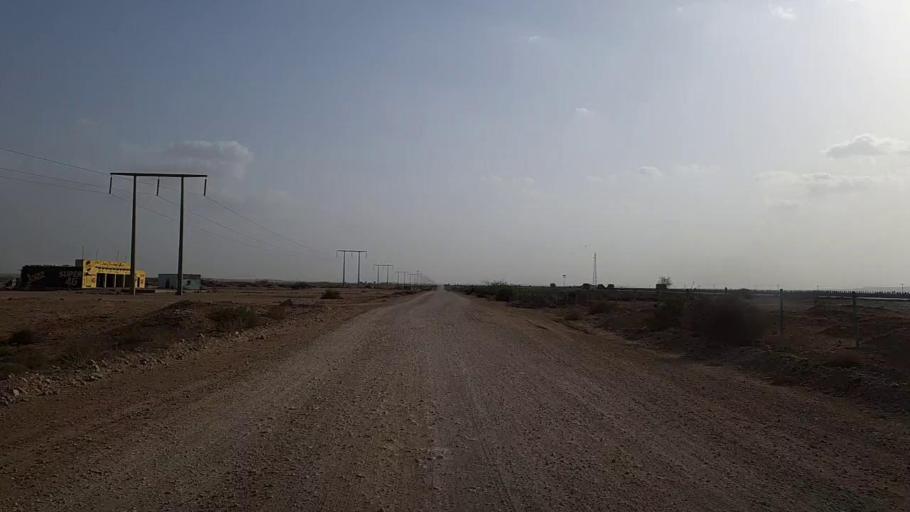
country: PK
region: Sindh
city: Kotri
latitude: 25.2216
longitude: 67.9146
